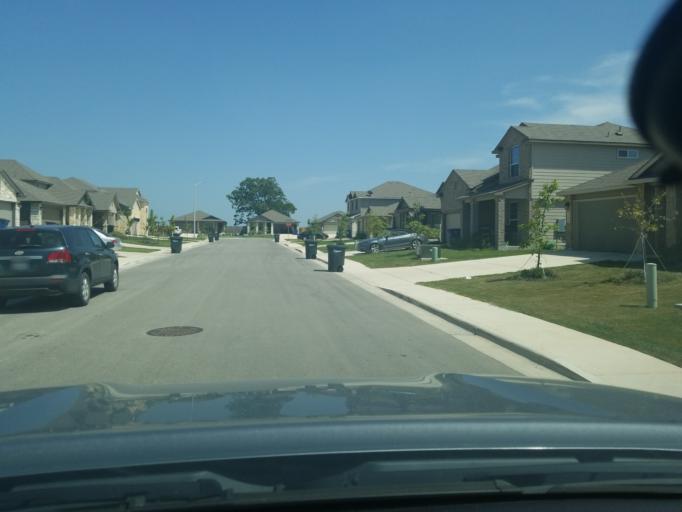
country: US
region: Texas
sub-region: Guadalupe County
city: Lake Dunlap
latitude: 29.6729
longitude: -98.0343
